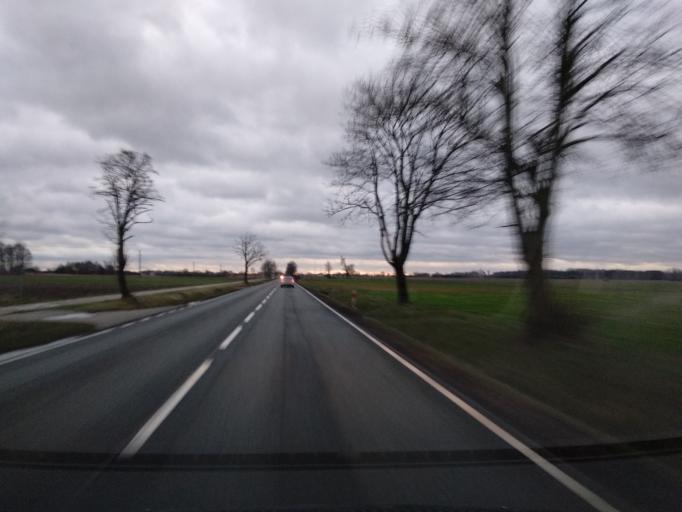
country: PL
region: Greater Poland Voivodeship
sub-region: Powiat koninski
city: Rychwal
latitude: 52.0925
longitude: 18.1653
